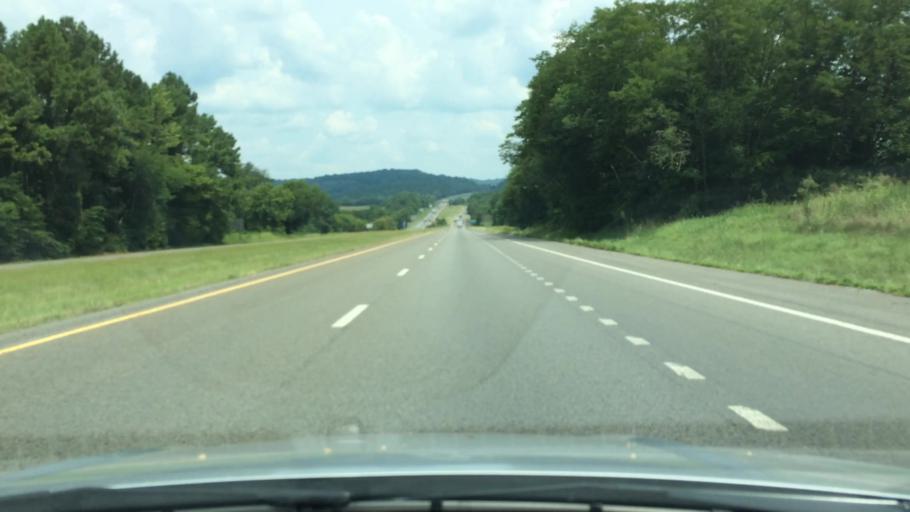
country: US
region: Tennessee
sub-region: Marshall County
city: Cornersville
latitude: 35.3124
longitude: -86.8822
